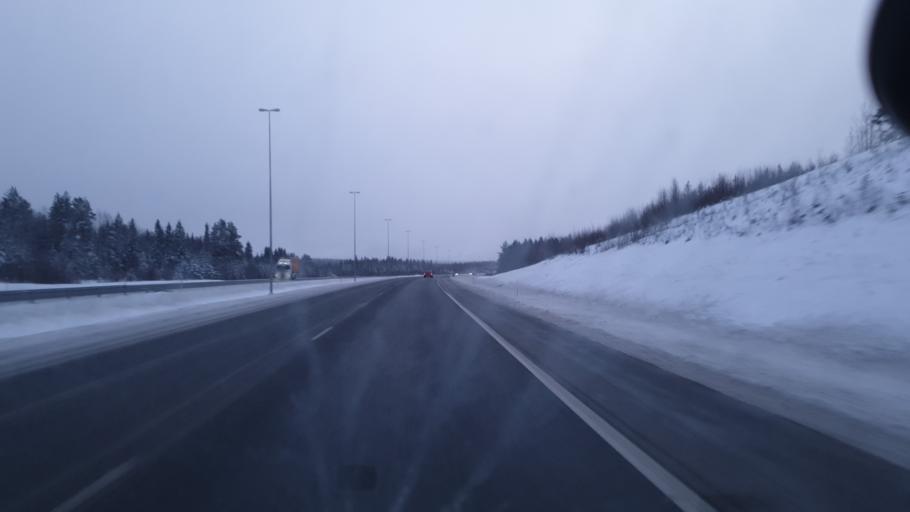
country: FI
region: Lapland
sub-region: Kemi-Tornio
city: Keminmaa
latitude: 65.8229
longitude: 24.4732
